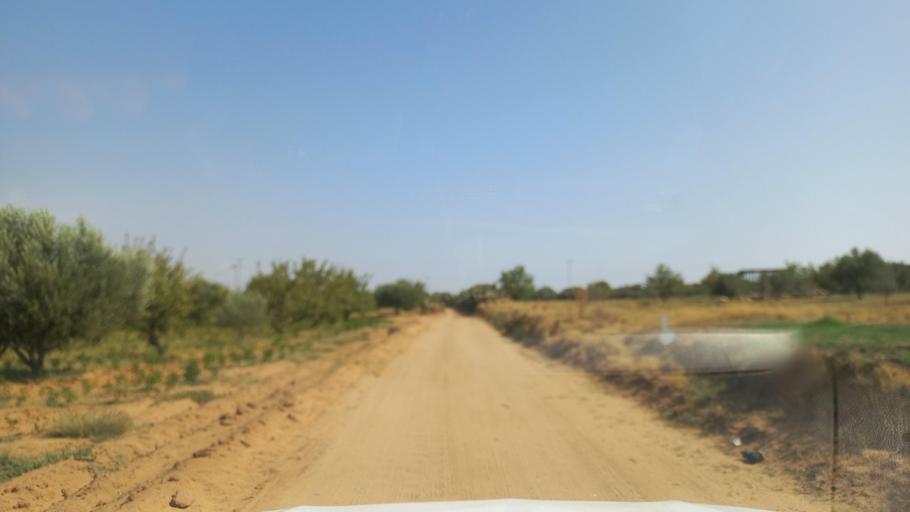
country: TN
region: Al Qasrayn
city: Kasserine
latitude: 35.2349
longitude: 9.0440
